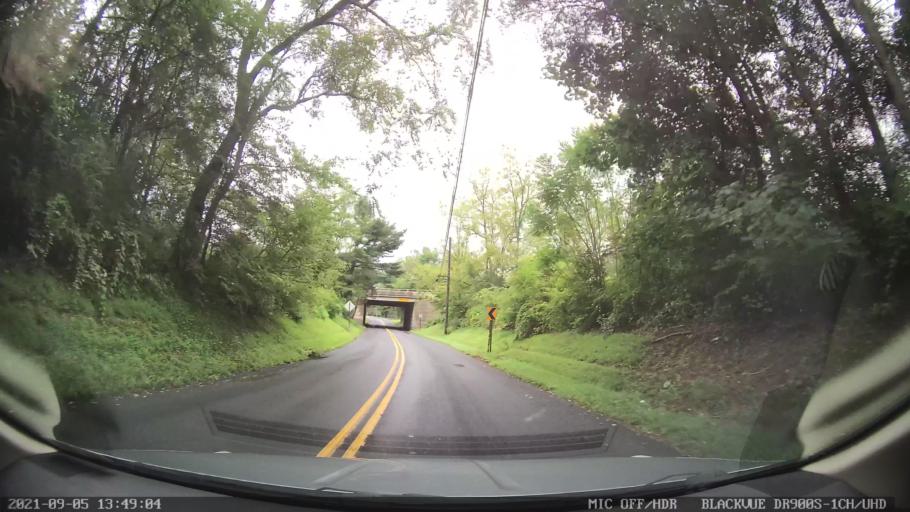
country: US
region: Pennsylvania
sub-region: Lehigh County
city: Schnecksville
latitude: 40.6280
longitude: -75.5779
